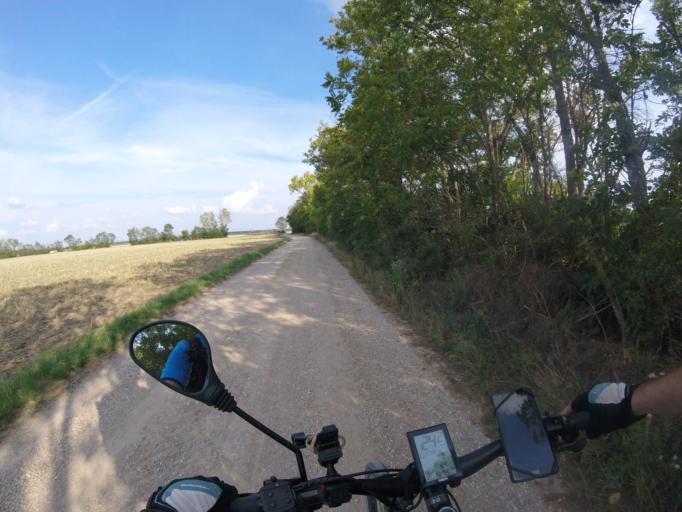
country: AT
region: Lower Austria
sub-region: Politischer Bezirk Baden
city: Trumau
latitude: 47.9872
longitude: 16.3461
